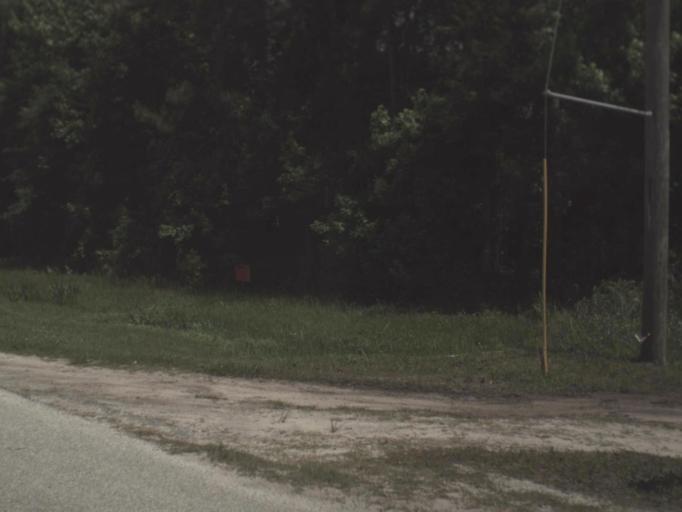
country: US
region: Florida
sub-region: Saint Johns County
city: Villano Beach
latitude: 29.9829
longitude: -81.3653
